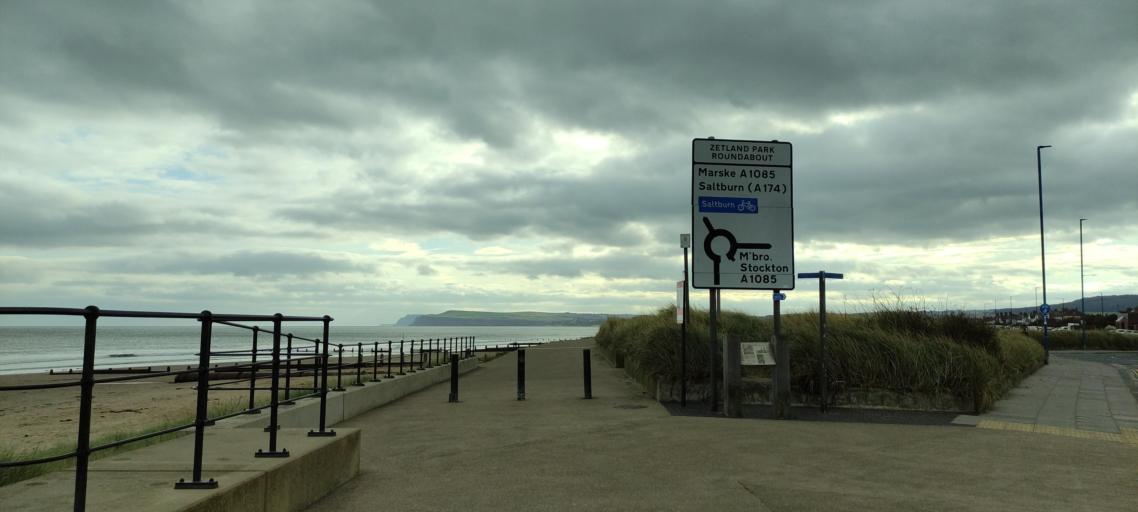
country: GB
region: England
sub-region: Redcar and Cleveland
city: Redcar
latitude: 54.6159
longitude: -1.0531
